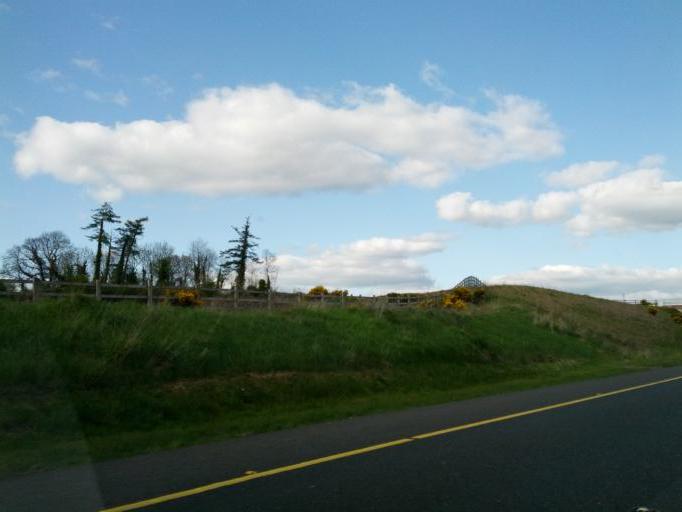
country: IE
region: Leinster
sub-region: An Iarmhi
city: Athlone
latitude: 53.4079
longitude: -8.0209
